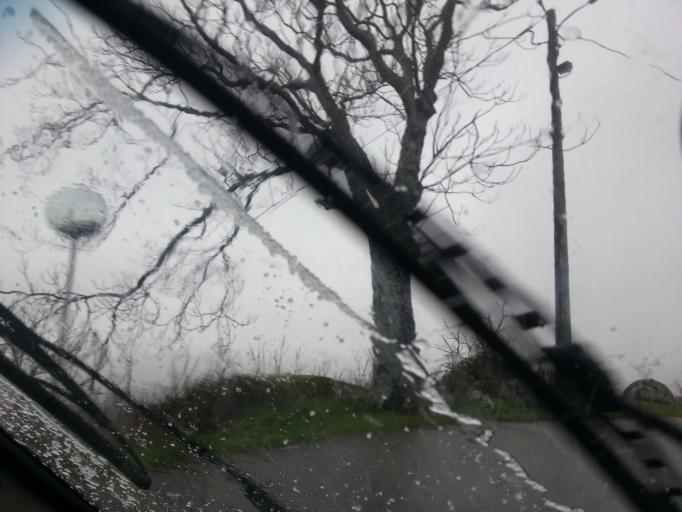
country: PT
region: Guarda
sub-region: Fornos de Algodres
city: Fornos de Algodres
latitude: 40.5407
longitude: -7.4643
